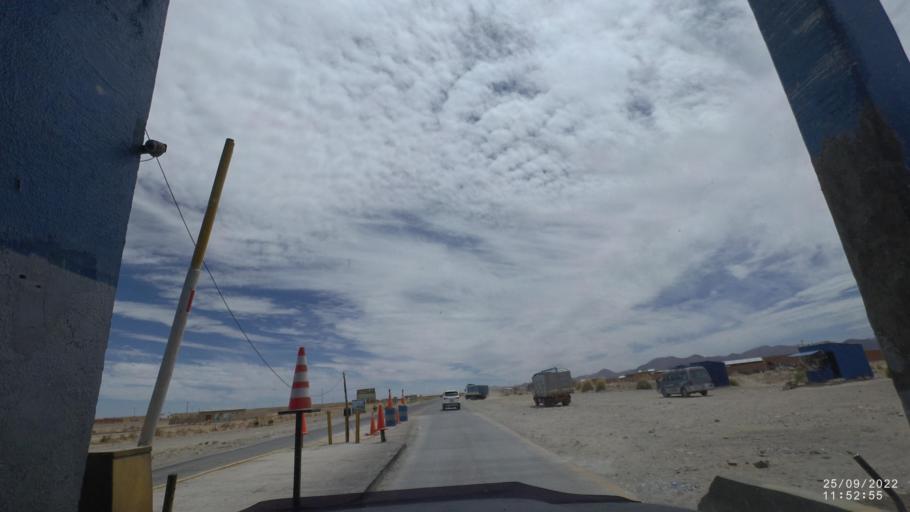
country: BO
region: Oruro
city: Challapata
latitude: -18.8901
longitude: -66.7815
